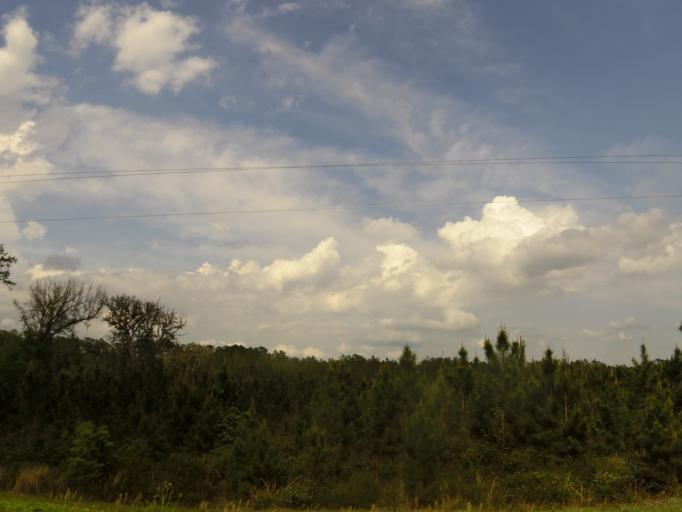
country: US
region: Georgia
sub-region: Charlton County
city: Folkston
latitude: 30.8034
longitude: -82.0317
